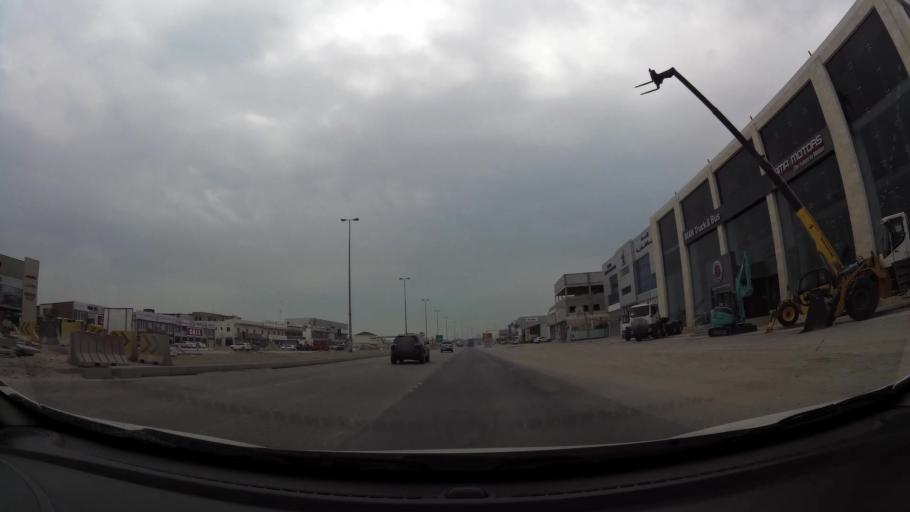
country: BH
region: Northern
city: Sitrah
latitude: 26.1355
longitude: 50.6062
